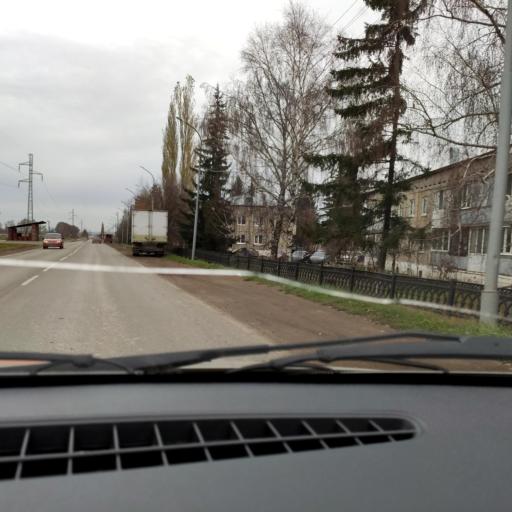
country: RU
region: Bashkortostan
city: Ufa
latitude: 54.8294
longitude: 55.9940
